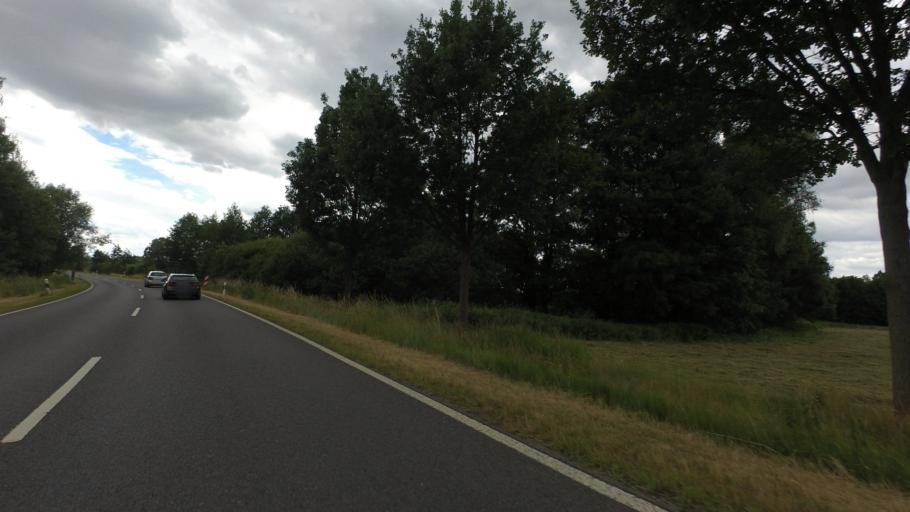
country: DE
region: Saxony
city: Wittichenau
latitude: 51.3879
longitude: 14.2360
